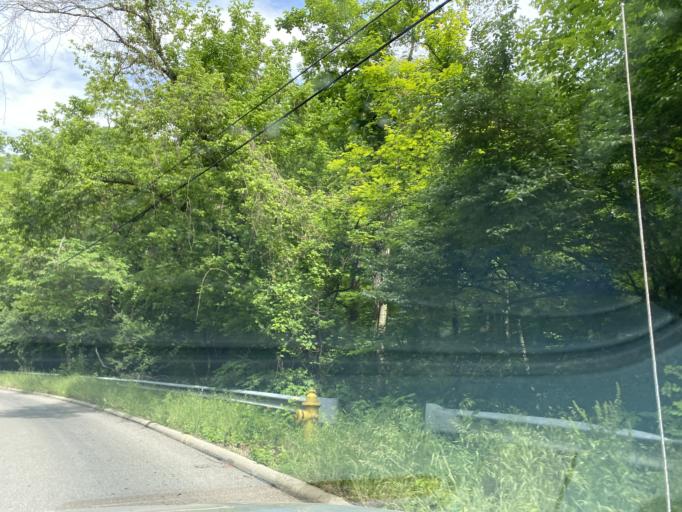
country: US
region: Ohio
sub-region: Hamilton County
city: Salem Heights
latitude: 39.0857
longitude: -84.4110
